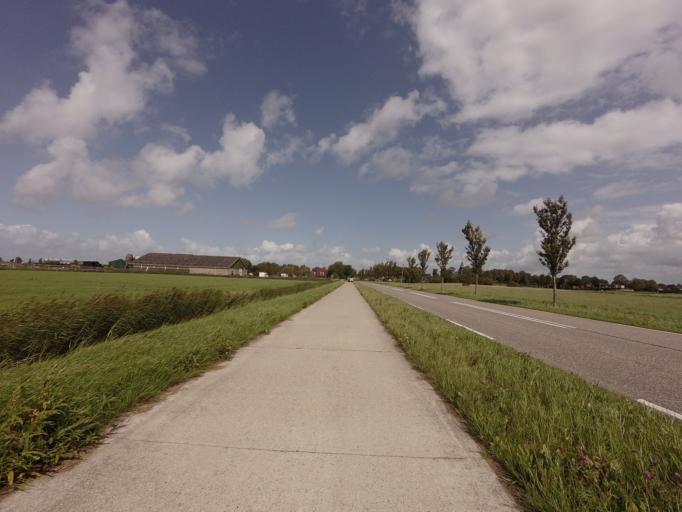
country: NL
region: Friesland
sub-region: Gemeente Harlingen
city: Harlingen
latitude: 53.1457
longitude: 5.4789
